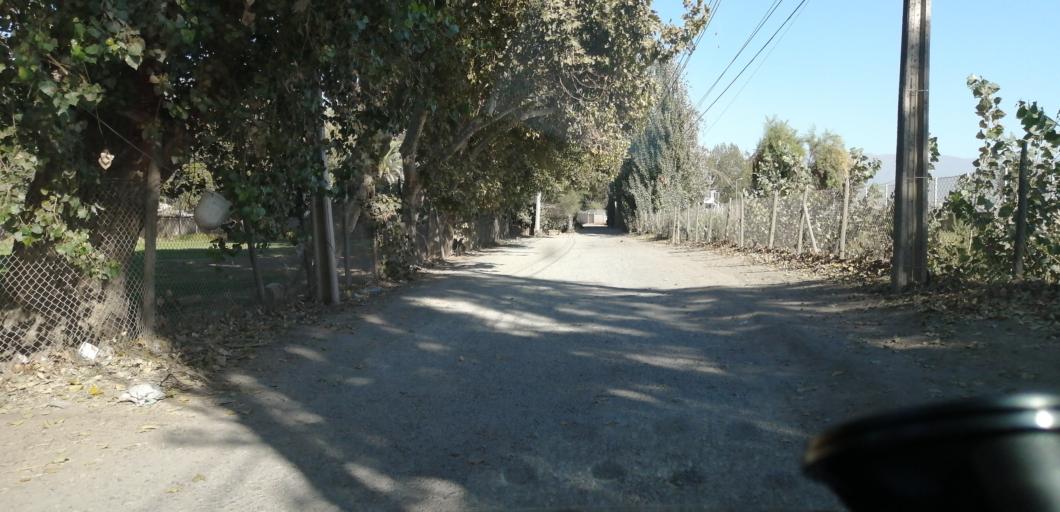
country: CL
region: Santiago Metropolitan
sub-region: Provincia de Santiago
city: Lo Prado
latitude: -33.4631
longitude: -70.7716
